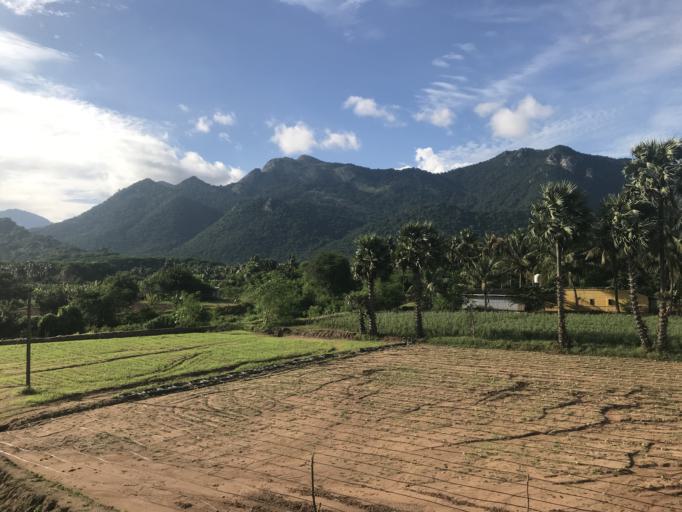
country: IN
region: Tamil Nadu
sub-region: Coimbatore
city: Madukkarai
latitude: 10.8790
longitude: 76.8649
